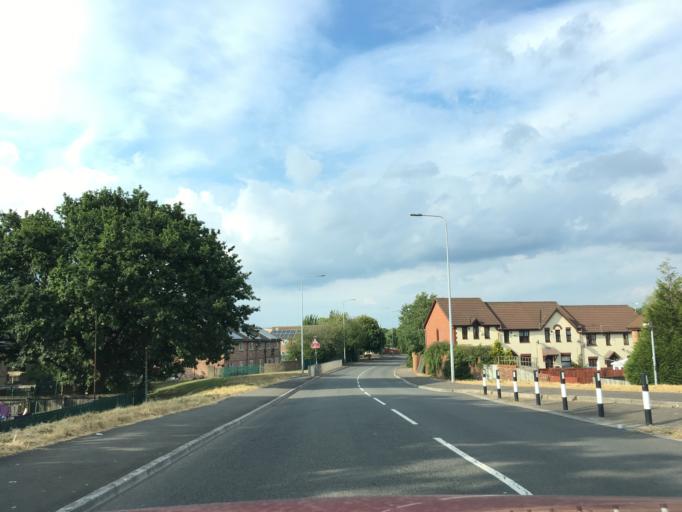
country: GB
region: Wales
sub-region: Newport
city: Marshfield
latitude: 51.5193
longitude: -3.0947
